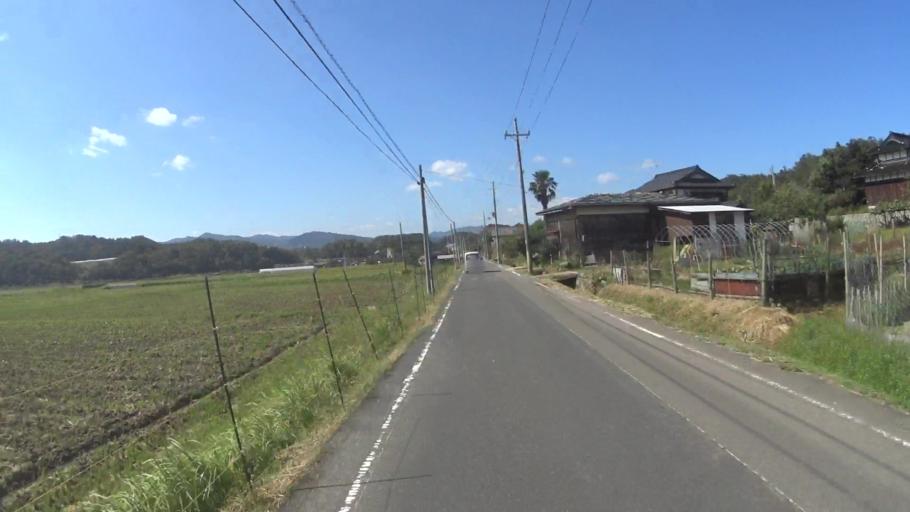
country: JP
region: Hyogo
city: Toyooka
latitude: 35.5942
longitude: 134.9640
